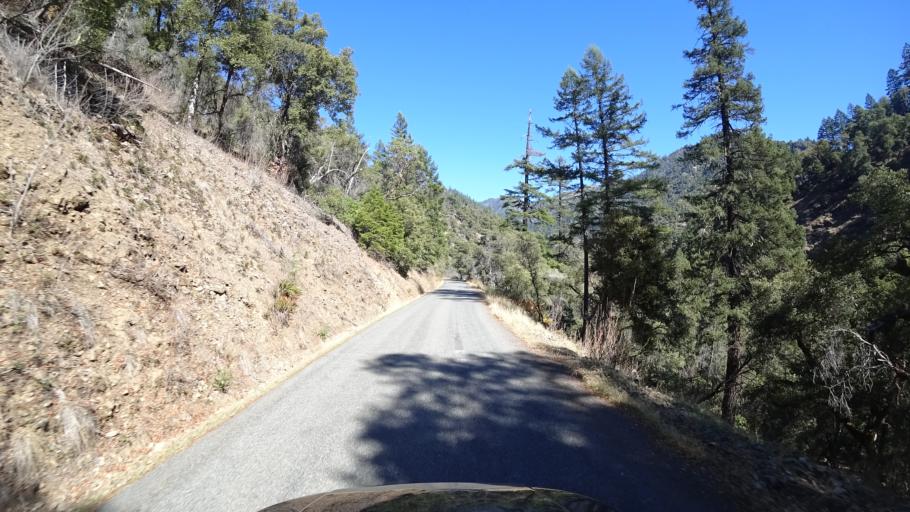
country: US
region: California
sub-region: Siskiyou County
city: Happy Camp
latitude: 41.3309
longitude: -123.3771
